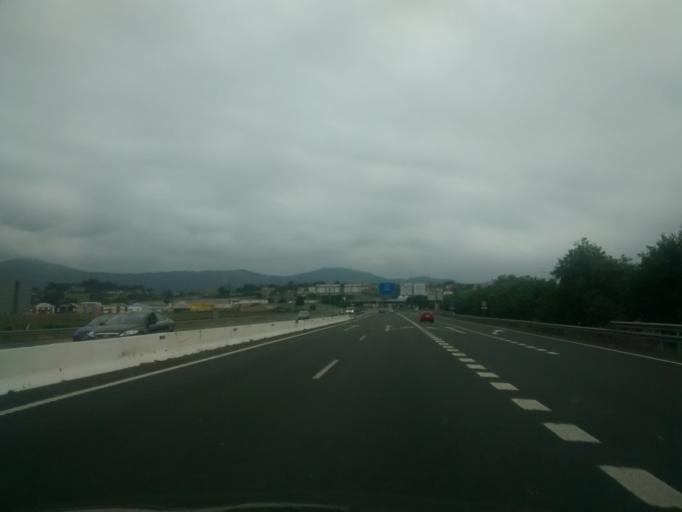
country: ES
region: Cantabria
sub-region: Provincia de Cantabria
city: El Astillero
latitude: 43.4303
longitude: -3.8365
